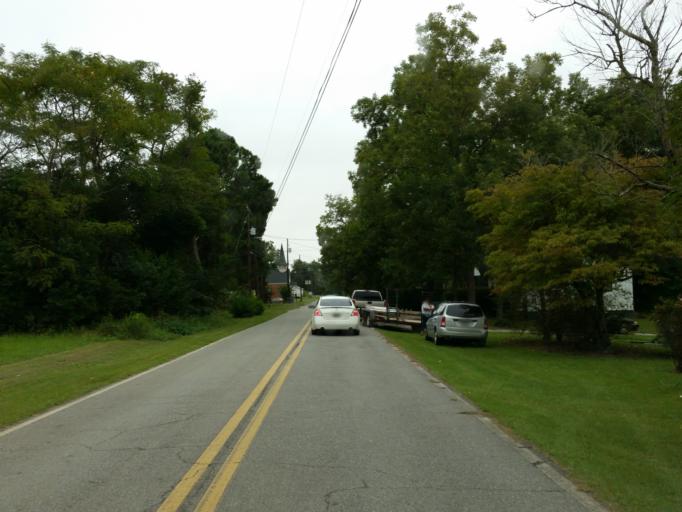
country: US
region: Georgia
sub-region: Dooly County
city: Unadilla
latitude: 32.2691
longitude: -83.7388
